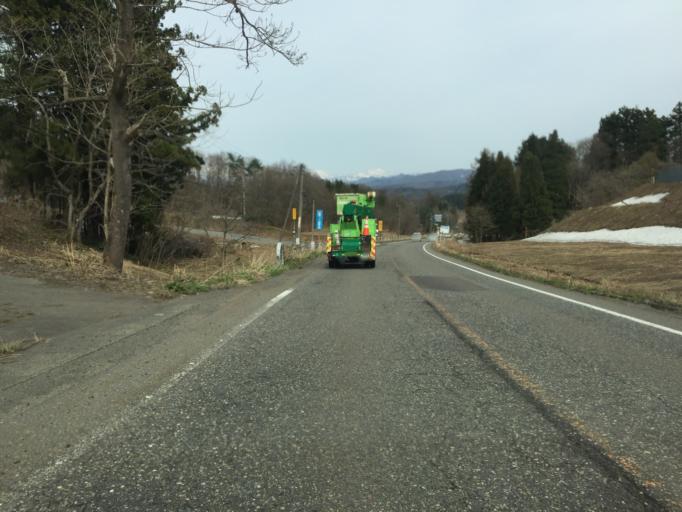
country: JP
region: Niigata
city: Tochio-honcho
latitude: 37.4520
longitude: 138.9558
